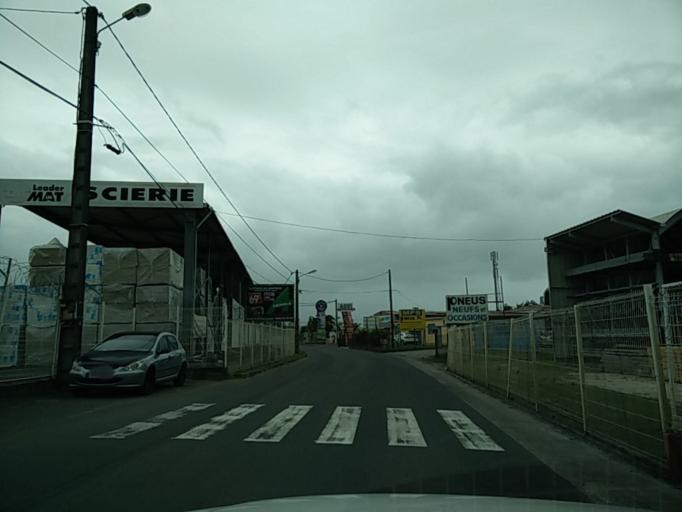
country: GP
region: Guadeloupe
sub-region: Guadeloupe
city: Pointe-a-Pitre
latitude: 16.2534
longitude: -61.5604
